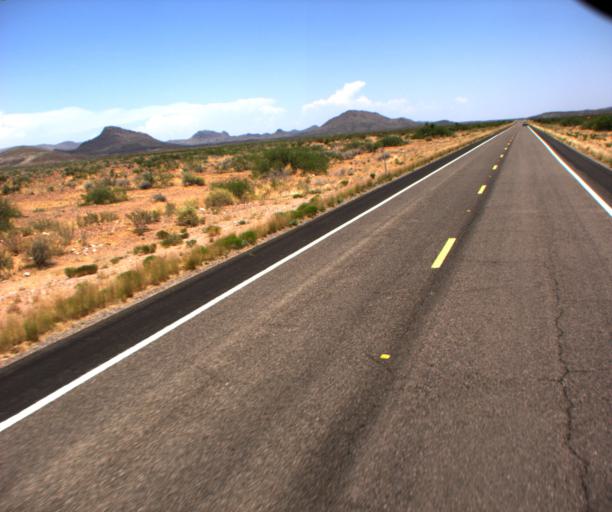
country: US
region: Arizona
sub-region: Graham County
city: Swift Trail Junction
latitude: 32.7635
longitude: -109.4496
